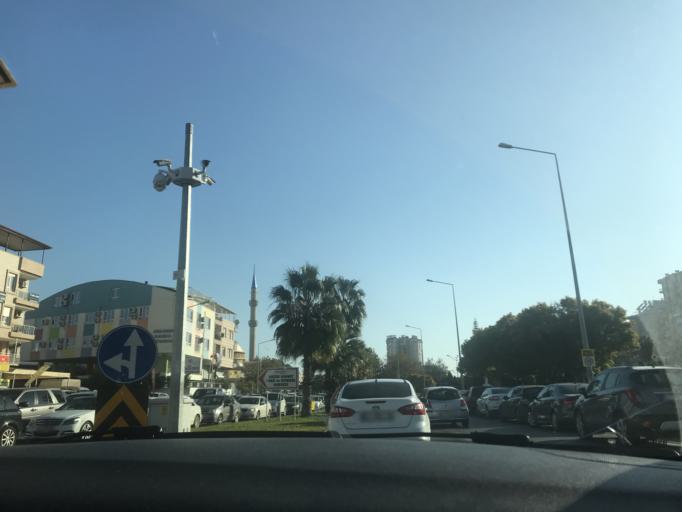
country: TR
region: Antalya
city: Antalya
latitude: 36.8836
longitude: 30.6483
